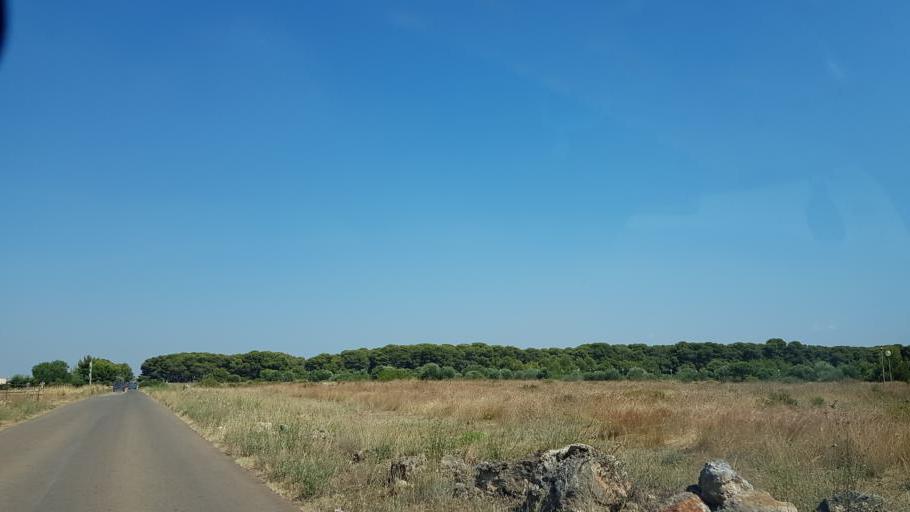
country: IT
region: Apulia
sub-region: Provincia di Lecce
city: Nardo
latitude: 40.1739
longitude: 17.9520
